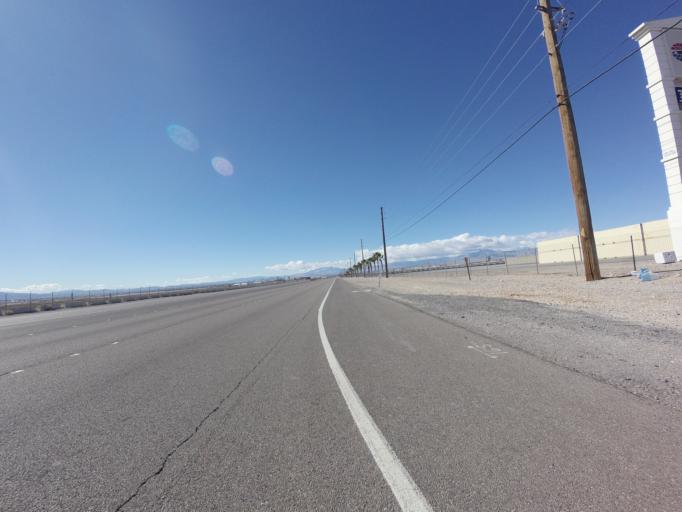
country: US
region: Nevada
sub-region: Clark County
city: Nellis Air Force Base
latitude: 36.2602
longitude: -115.0208
